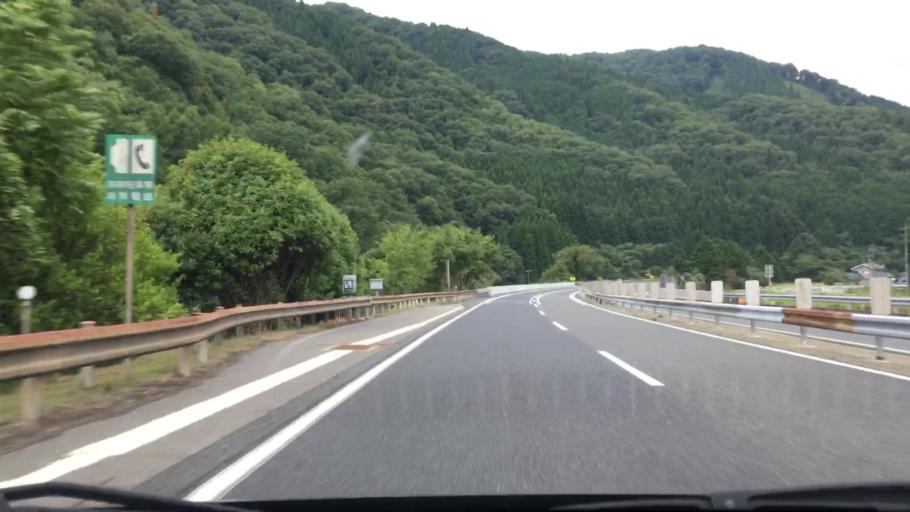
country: JP
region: Okayama
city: Niimi
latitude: 35.0079
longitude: 133.4908
